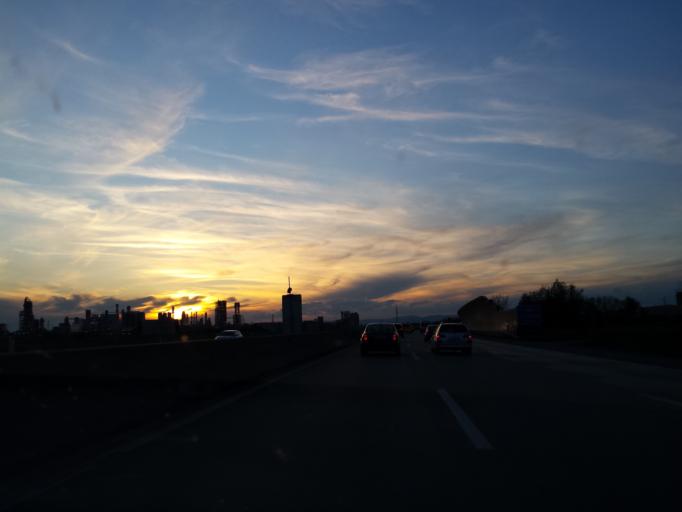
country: AT
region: Lower Austria
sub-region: Politischer Bezirk Wien-Umgebung
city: Rauchenwarth
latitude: 48.1357
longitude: 16.5294
